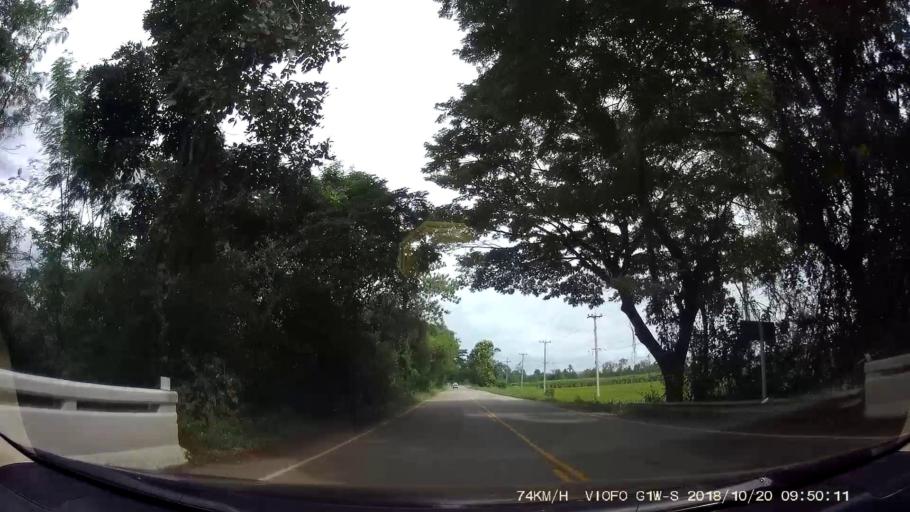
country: TH
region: Chaiyaphum
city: Khon San
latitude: 16.5282
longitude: 101.9029
